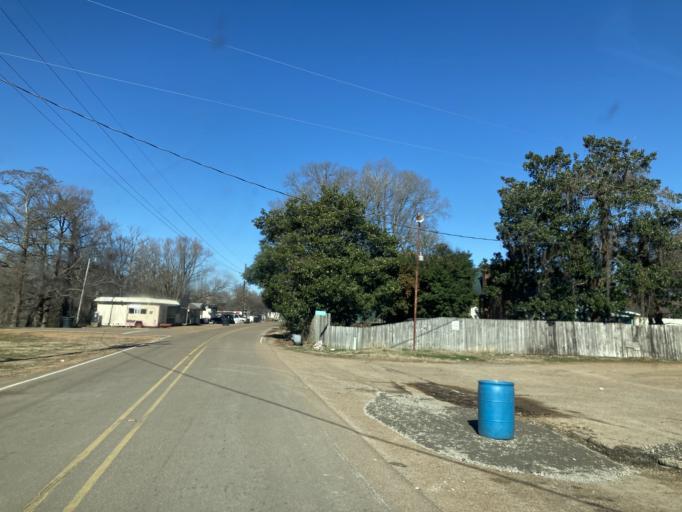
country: US
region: Mississippi
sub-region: Yazoo County
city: Yazoo City
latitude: 32.9780
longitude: -90.5911
